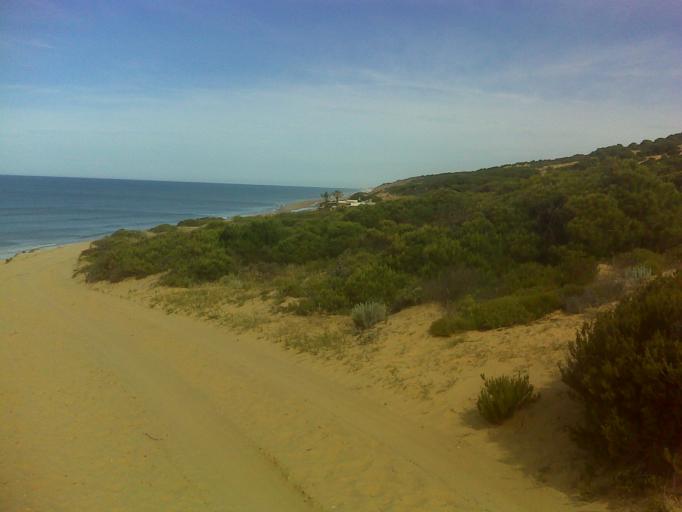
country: ES
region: Andalusia
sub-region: Provincia de Huelva
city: Mazagon
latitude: 37.0146
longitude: -6.5803
